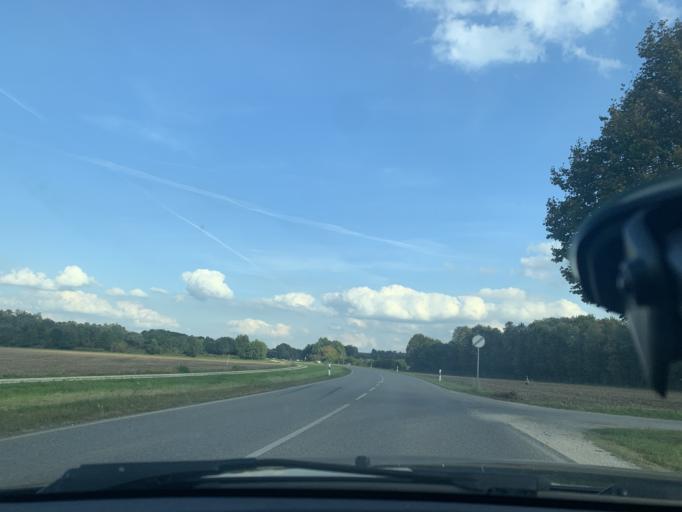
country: DE
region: Bavaria
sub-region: Swabia
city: Friedberg
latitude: 48.3402
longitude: 10.9705
